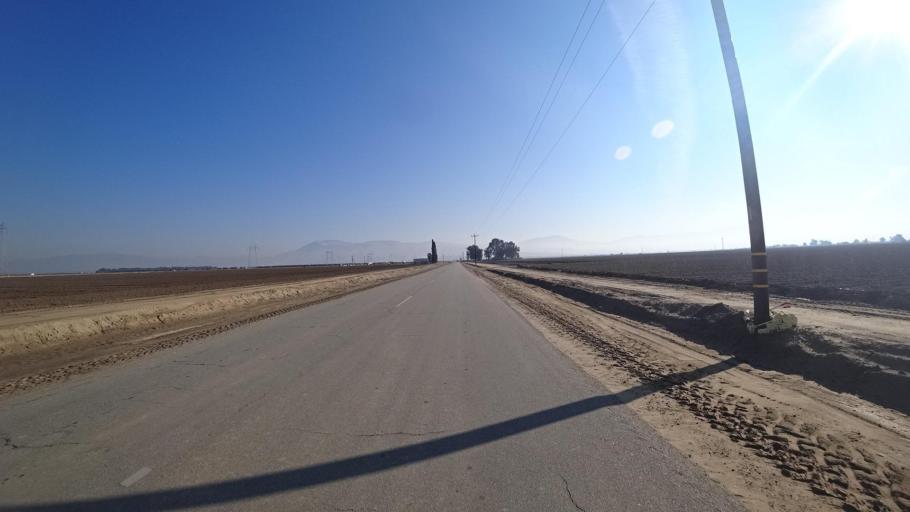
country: US
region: California
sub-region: Kern County
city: Weedpatch
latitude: 35.1219
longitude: -118.9289
